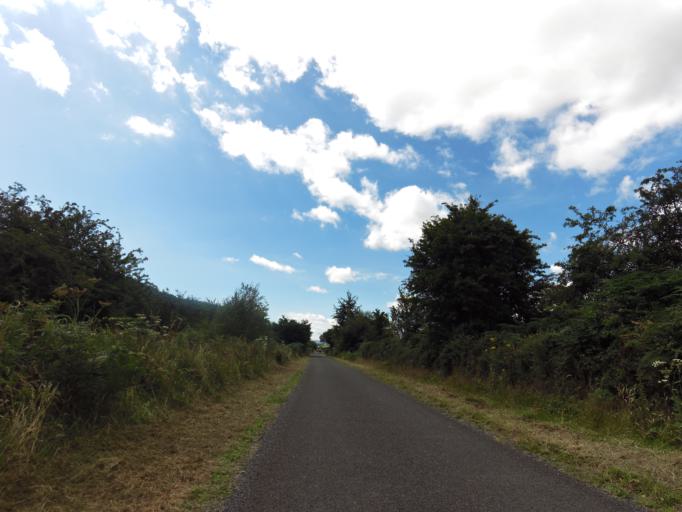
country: IE
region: Leinster
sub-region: Kilkenny
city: Mooncoin
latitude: 52.2385
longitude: -7.2716
